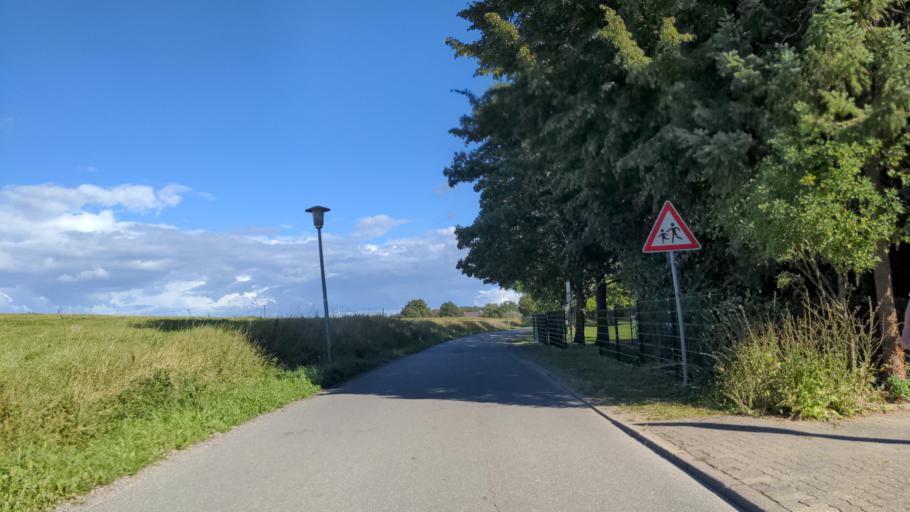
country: DE
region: Schleswig-Holstein
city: Gromitz
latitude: 54.1726
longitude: 10.9409
